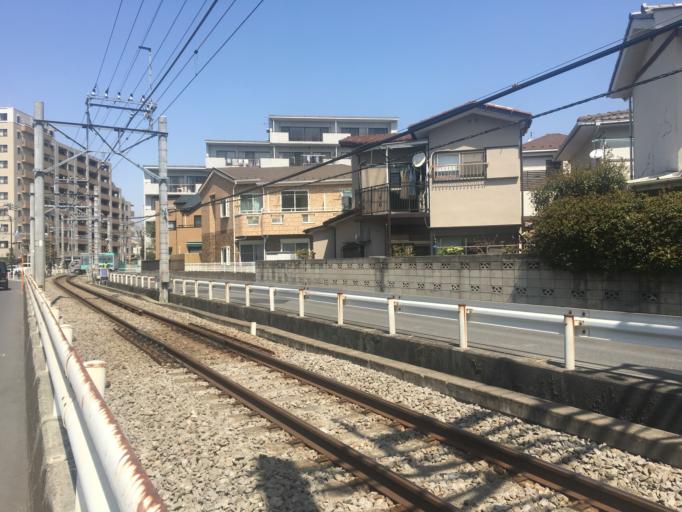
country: JP
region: Tokyo
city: Kokubunji
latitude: 35.7043
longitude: 139.4778
